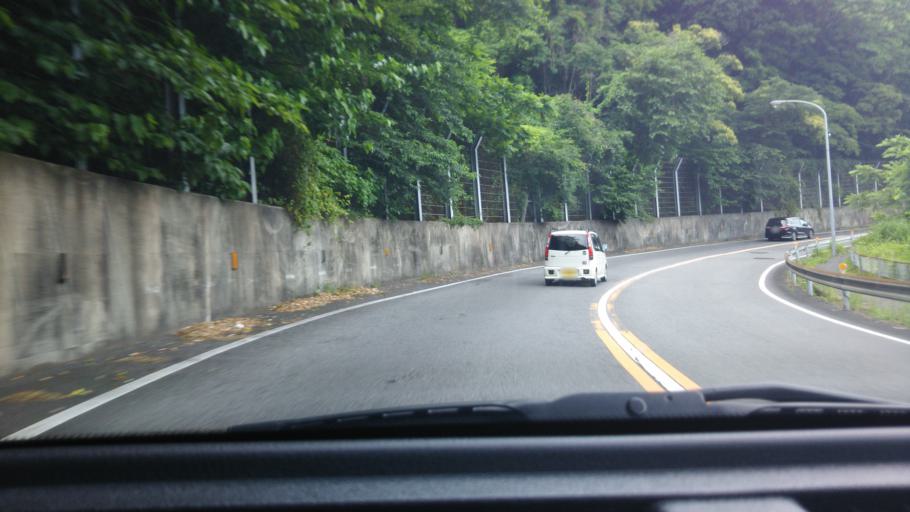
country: JP
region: Shizuoka
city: Ito
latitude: 34.8721
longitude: 139.0956
